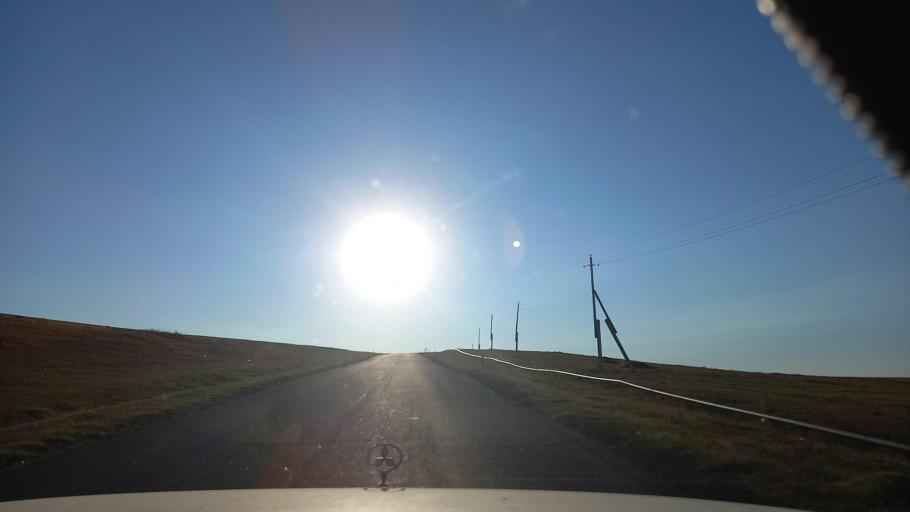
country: AZ
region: Shamkir Rayon
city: Shamkhor
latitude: 40.7661
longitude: 45.9480
